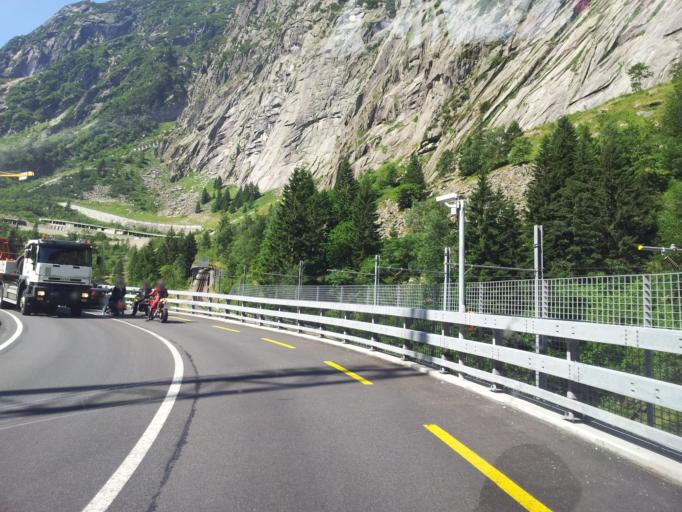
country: CH
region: Uri
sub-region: Uri
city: Andermatt
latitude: 46.6609
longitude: 8.5862
